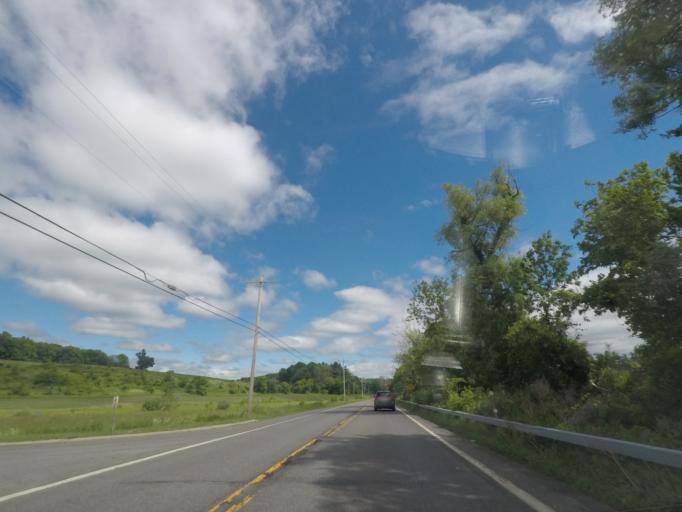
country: US
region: New York
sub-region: Columbia County
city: Philmont
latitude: 42.2125
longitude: -73.7033
